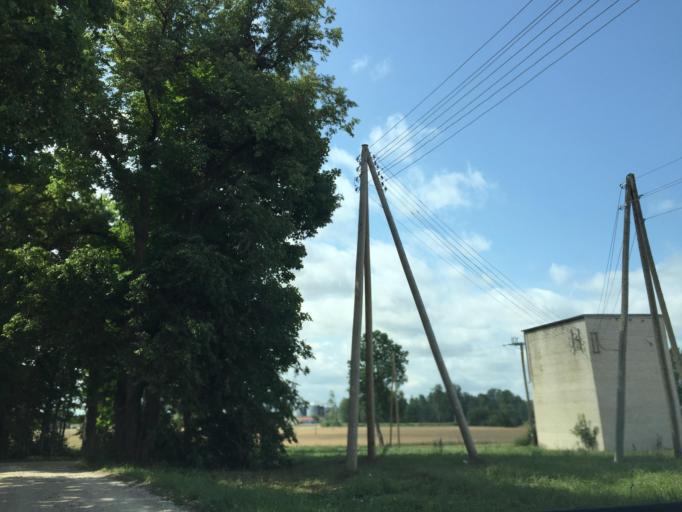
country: LV
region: Kandava
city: Kandava
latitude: 56.9737
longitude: 22.9285
